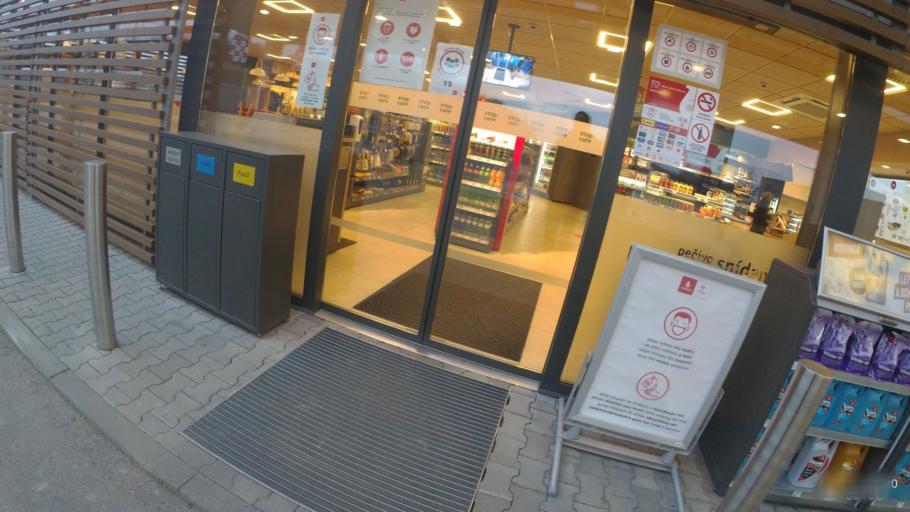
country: CZ
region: Plzensky
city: Dobrany
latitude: 49.6784
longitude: 13.3311
